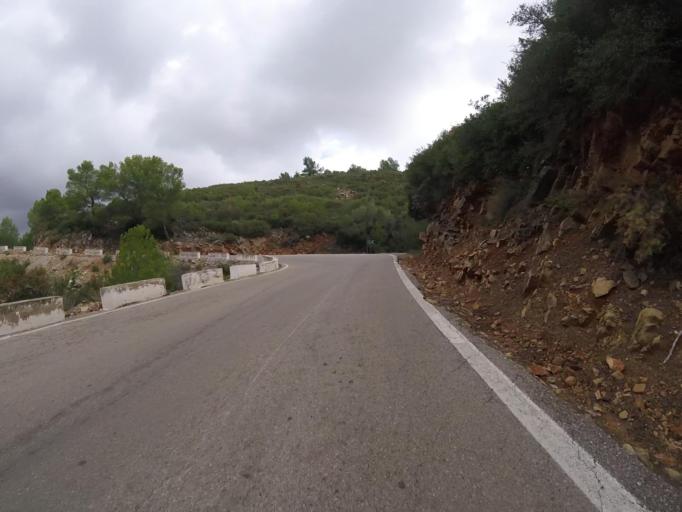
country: ES
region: Valencia
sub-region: Provincia de Castello
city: Cabanes
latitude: 40.1447
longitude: 0.0889
